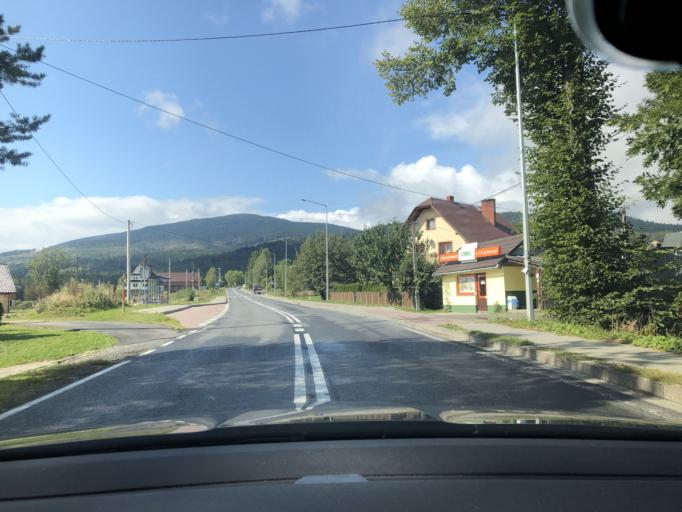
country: PL
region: Lesser Poland Voivodeship
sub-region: Powiat nowotarski
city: Zubrzyca Gorna
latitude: 49.5800
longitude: 19.6232
